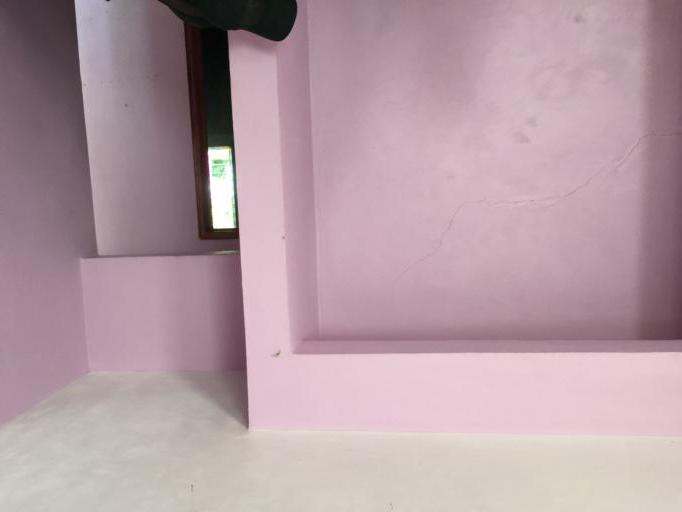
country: MX
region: Mexico
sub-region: Ocuilan
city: Plaza Nueva
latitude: 18.9217
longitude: -99.4392
